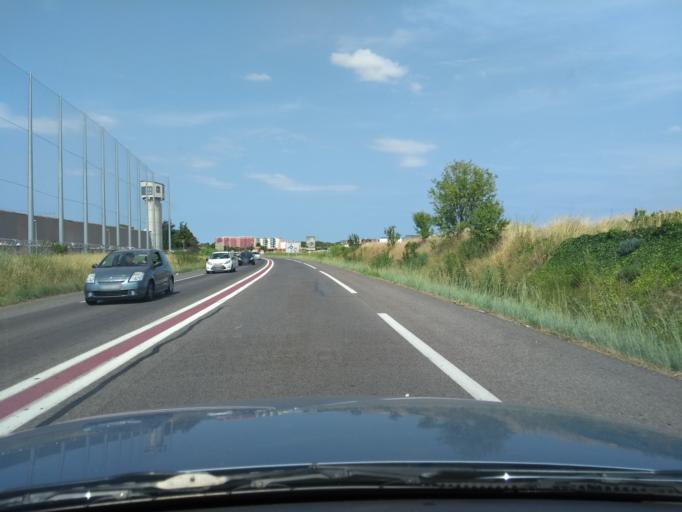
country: FR
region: Languedoc-Roussillon
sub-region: Departement des Pyrenees-Orientales
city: Perpignan
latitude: 42.6788
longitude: 2.8723
